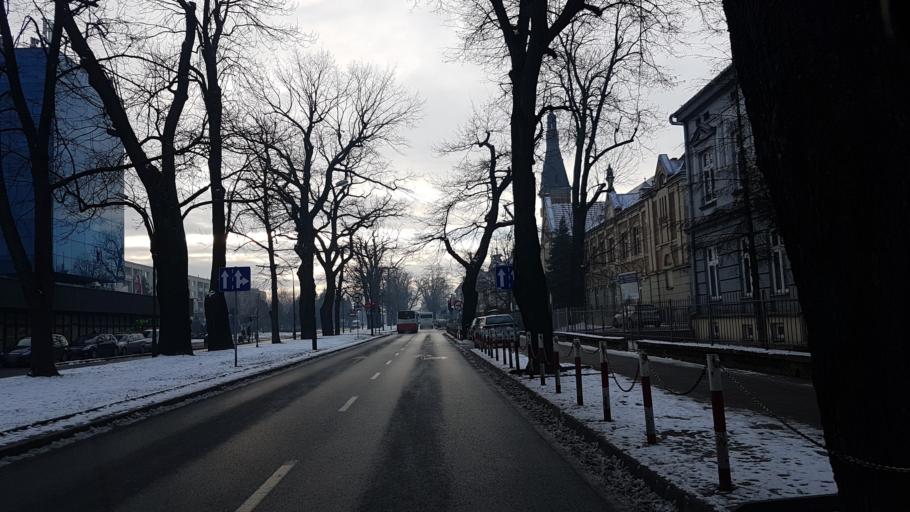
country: PL
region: Lesser Poland Voivodeship
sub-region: Powiat nowosadecki
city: Nowy Sacz
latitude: 49.6102
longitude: 20.7002
